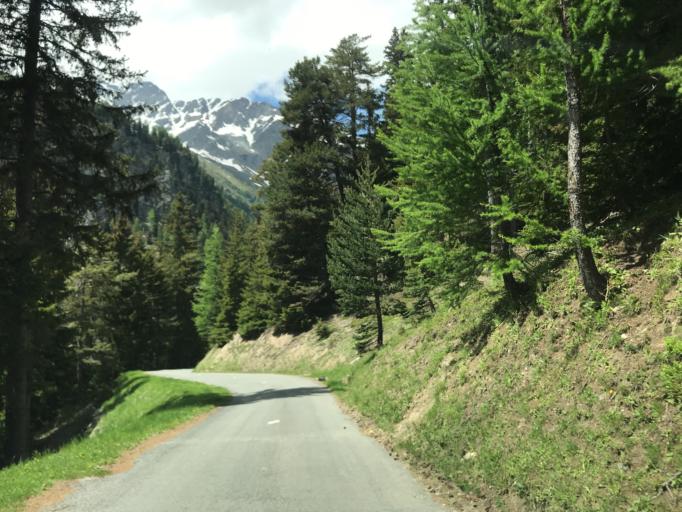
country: FR
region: Rhone-Alpes
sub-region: Departement de la Savoie
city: Modane
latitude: 45.2214
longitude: 6.6546
